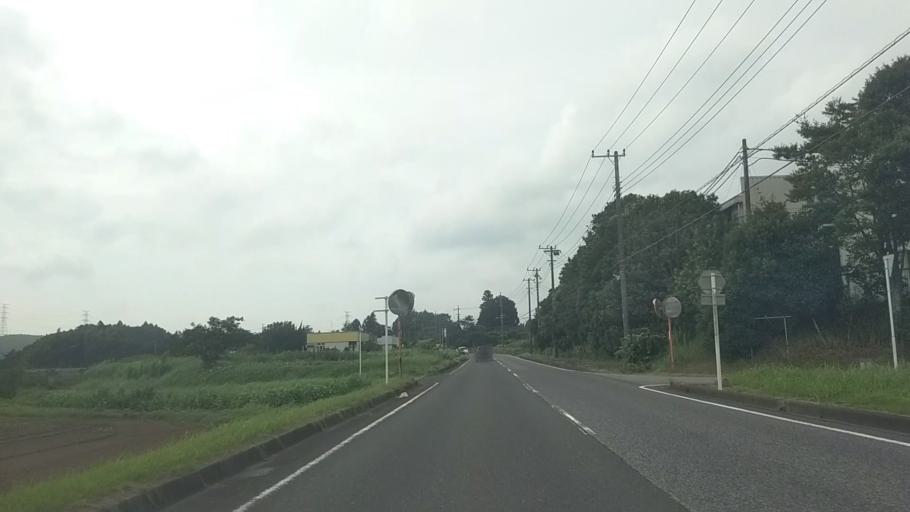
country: JP
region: Chiba
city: Kimitsu
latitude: 35.2755
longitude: 139.9942
